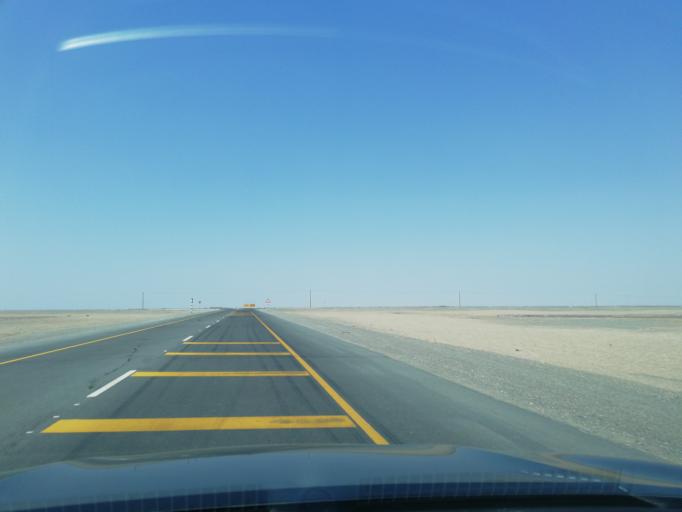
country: OM
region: Muhafazat ad Dakhiliyah
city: Adam
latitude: 22.2473
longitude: 58.0932
